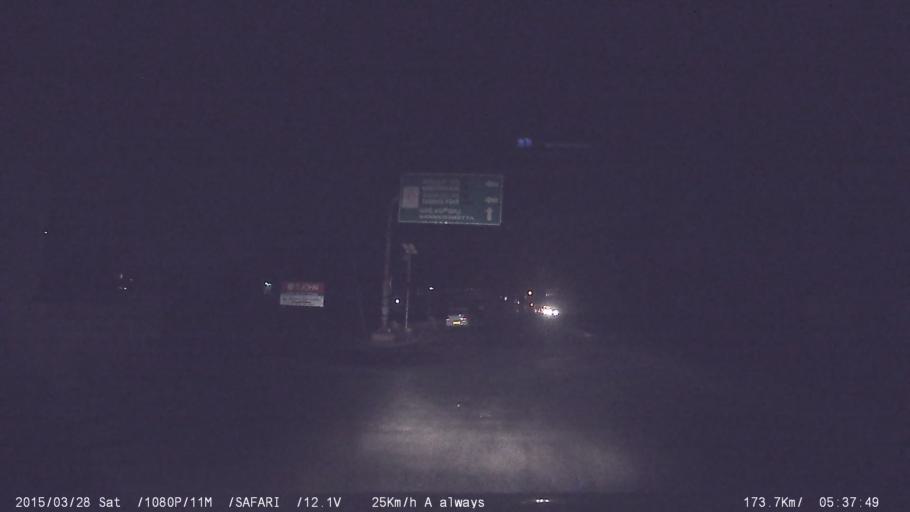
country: IN
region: Karnataka
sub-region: Bangalore Urban
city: Bangalore
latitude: 12.8499
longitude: 77.5884
